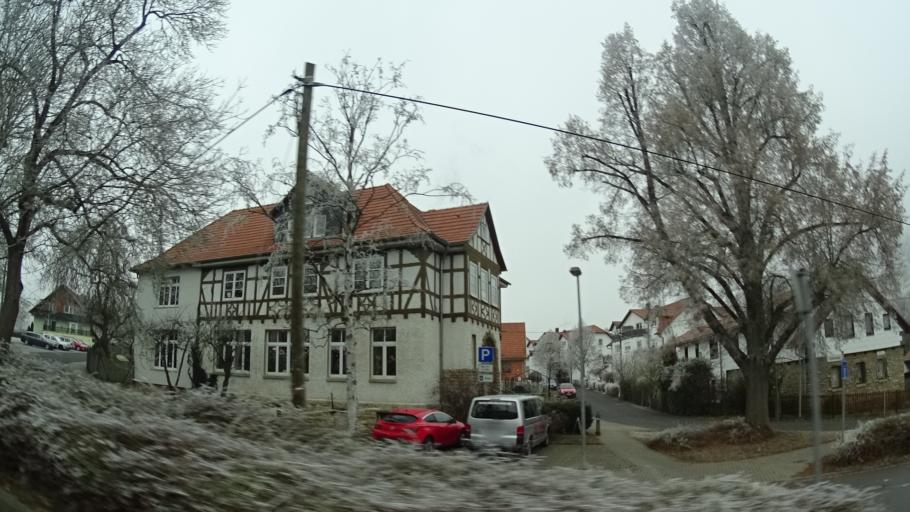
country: DE
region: Thuringia
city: Sulzfeld
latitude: 50.5233
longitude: 10.3536
